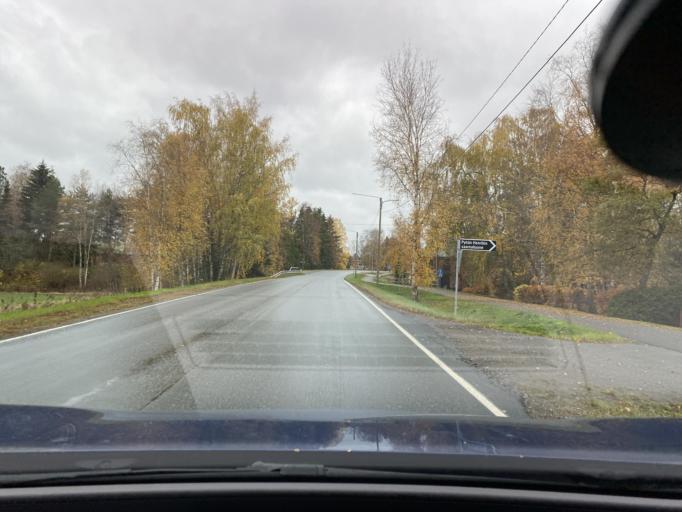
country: FI
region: Satakunta
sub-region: Pori
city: Kokemaeki
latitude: 61.2573
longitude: 22.3712
